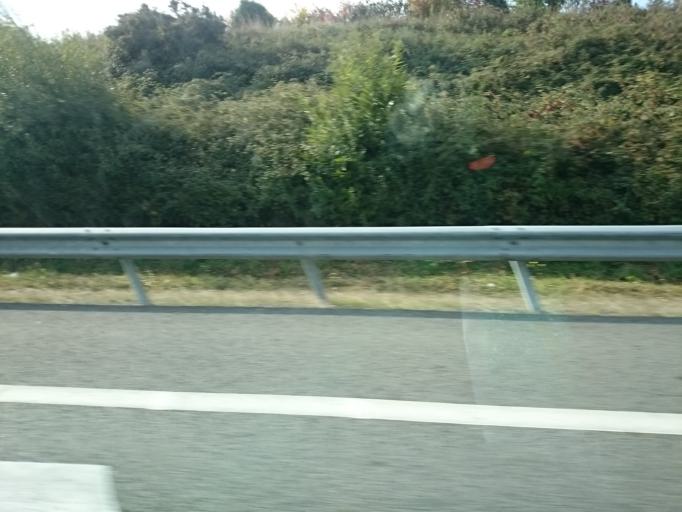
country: FR
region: Brittany
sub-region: Departement d'Ille-et-Vilaine
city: Grand-Fougeray
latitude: 47.7488
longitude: -1.7155
